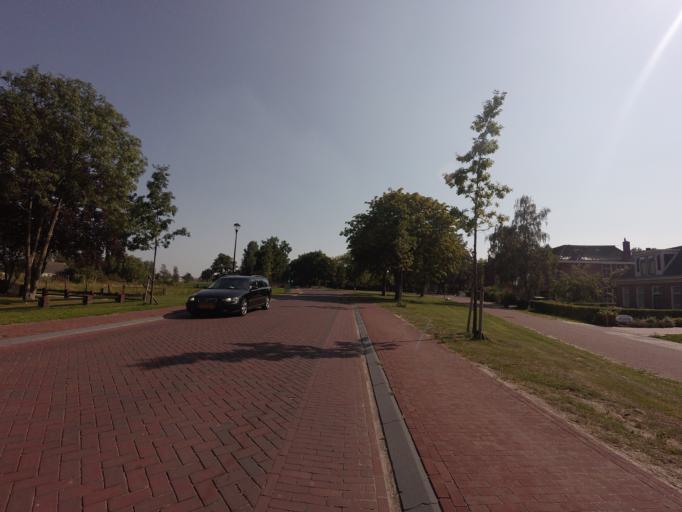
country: NL
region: Groningen
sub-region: Gemeente Zuidhorn
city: Zuidhorn
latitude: 53.2542
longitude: 6.4004
